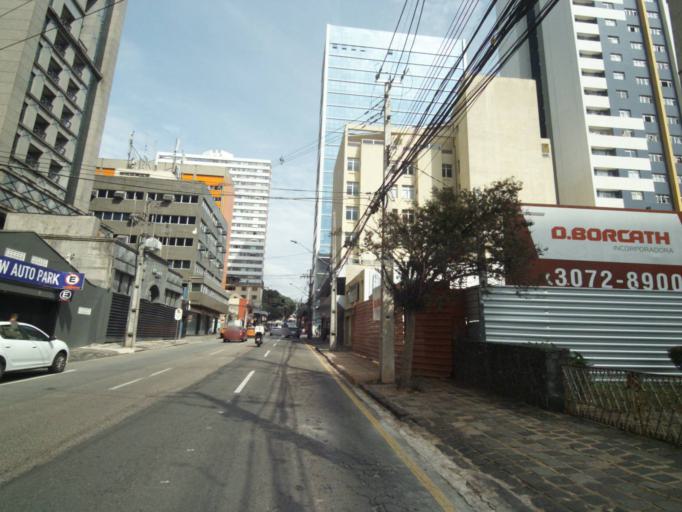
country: BR
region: Parana
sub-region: Curitiba
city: Curitiba
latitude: -25.4375
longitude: -49.2780
